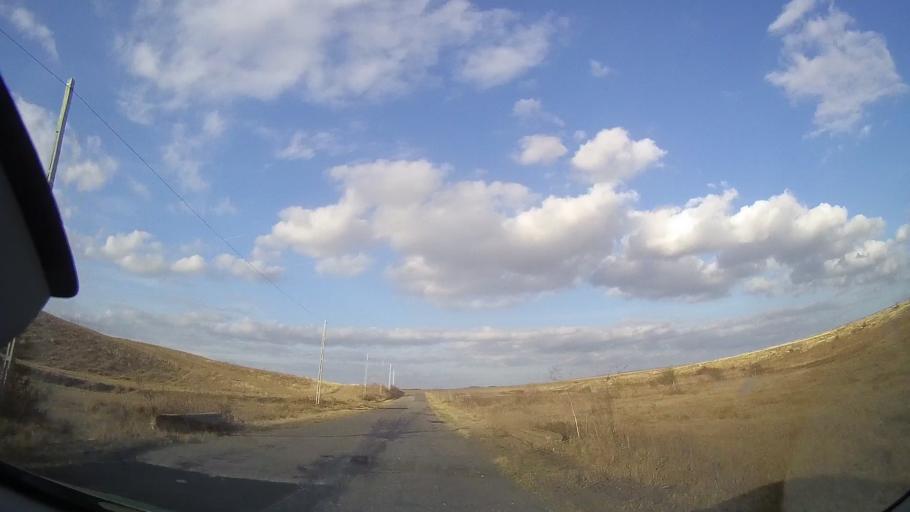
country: RO
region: Constanta
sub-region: Comuna Cerchezu
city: Cerchezu
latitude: 43.8405
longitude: 28.0980
